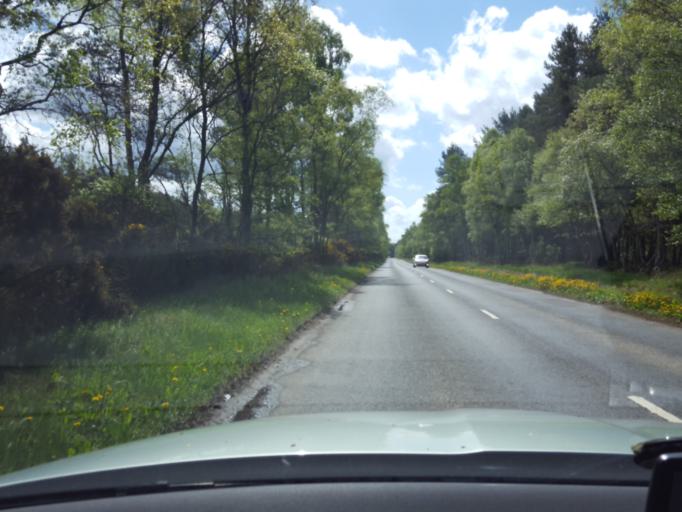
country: GB
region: Scotland
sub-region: Angus
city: Brechin
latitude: 56.7996
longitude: -2.6507
